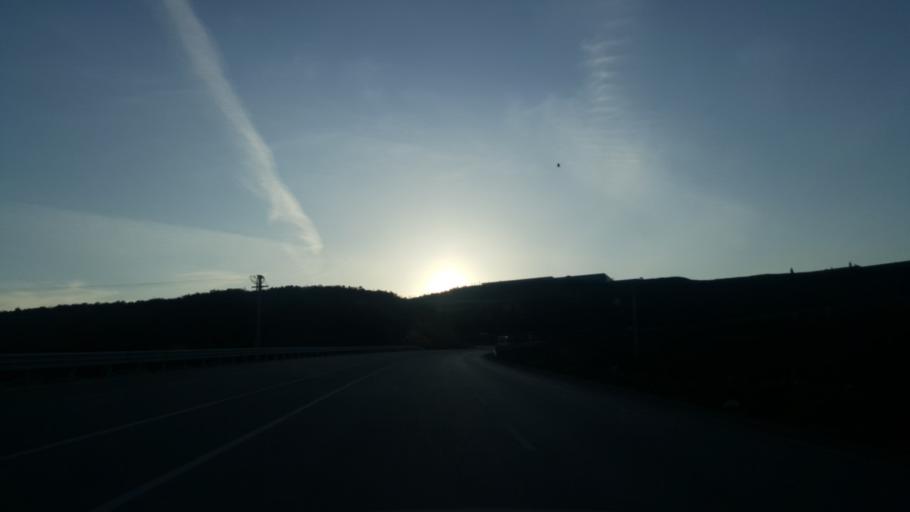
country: TR
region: Kocaeli
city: Tavsanli
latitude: 40.8422
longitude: 29.5459
